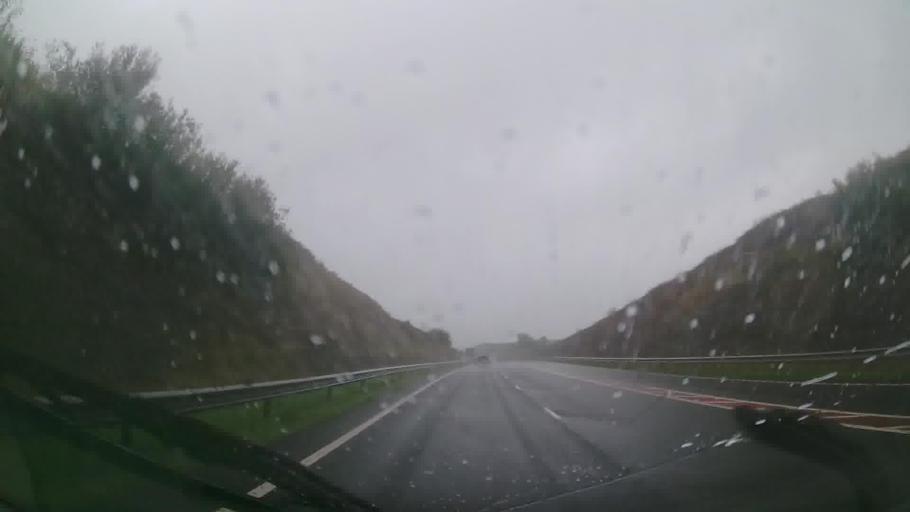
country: GB
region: Wales
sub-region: Carmarthenshire
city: Llanddowror
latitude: 51.8015
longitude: -4.5445
